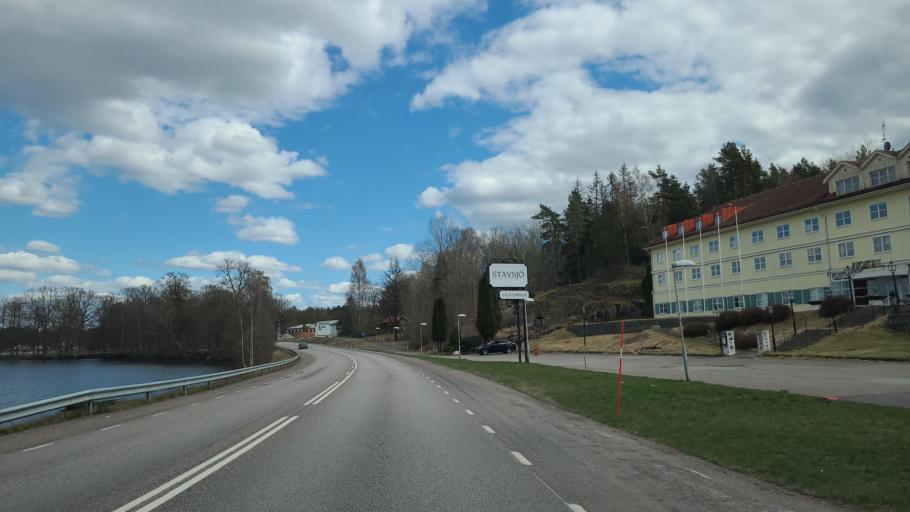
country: SE
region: OEstergoetland
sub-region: Norrkopings Kommun
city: Krokek
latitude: 58.7246
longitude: 16.4172
